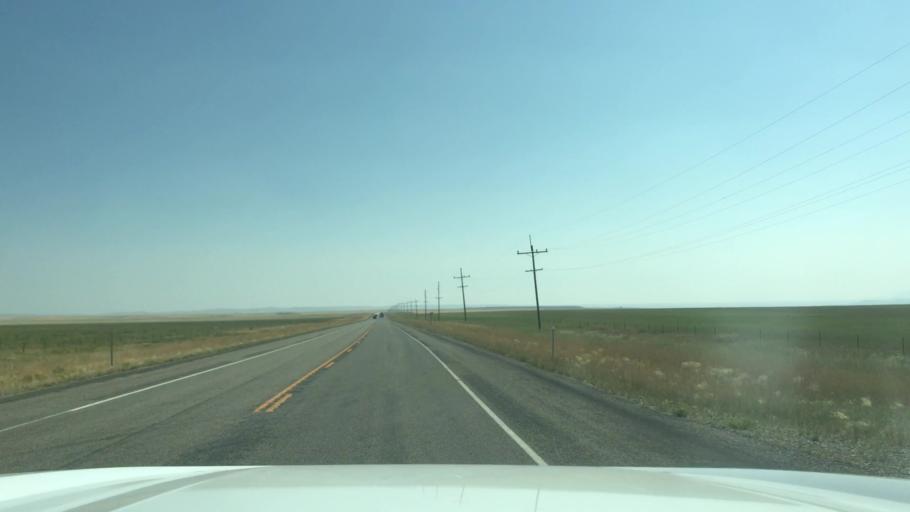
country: US
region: Montana
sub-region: Wheatland County
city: Harlowton
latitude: 46.5191
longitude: -109.7660
